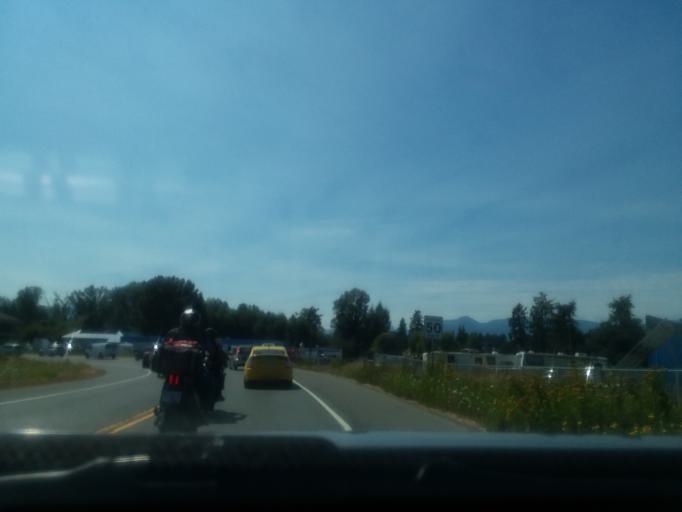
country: CA
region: British Columbia
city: Courtenay
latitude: 49.6943
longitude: -124.9902
